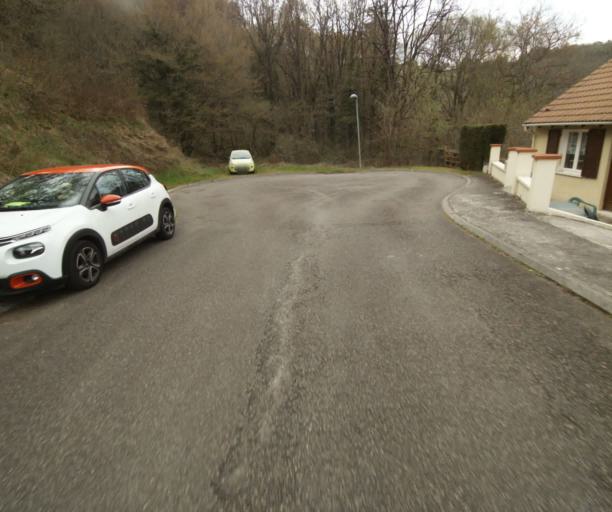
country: FR
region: Limousin
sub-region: Departement de la Correze
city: Laguenne
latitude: 45.2534
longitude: 1.7745
